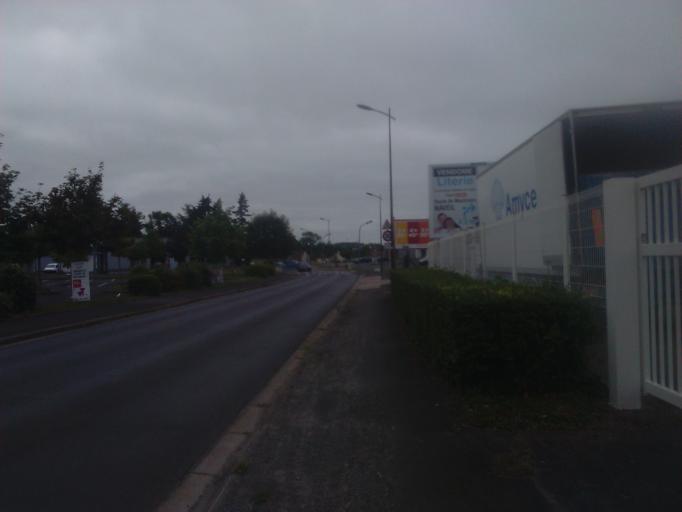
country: FR
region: Centre
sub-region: Departement du Loir-et-Cher
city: Naveil
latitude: 47.8000
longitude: 1.0471
